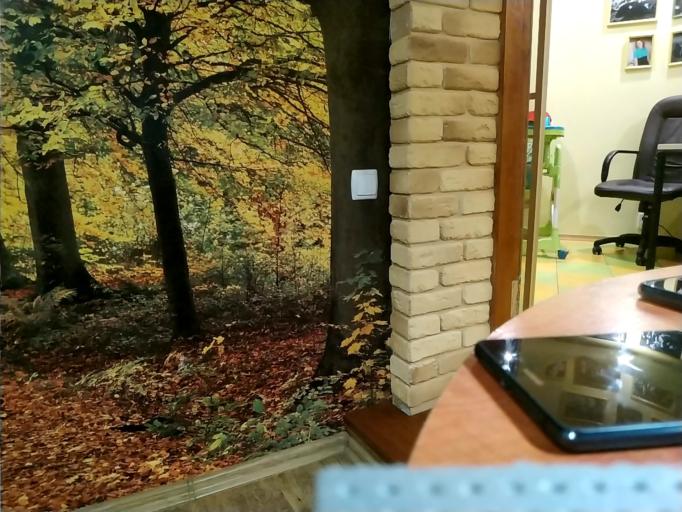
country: RU
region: Tverskaya
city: Zubtsov
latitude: 56.2065
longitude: 34.7153
